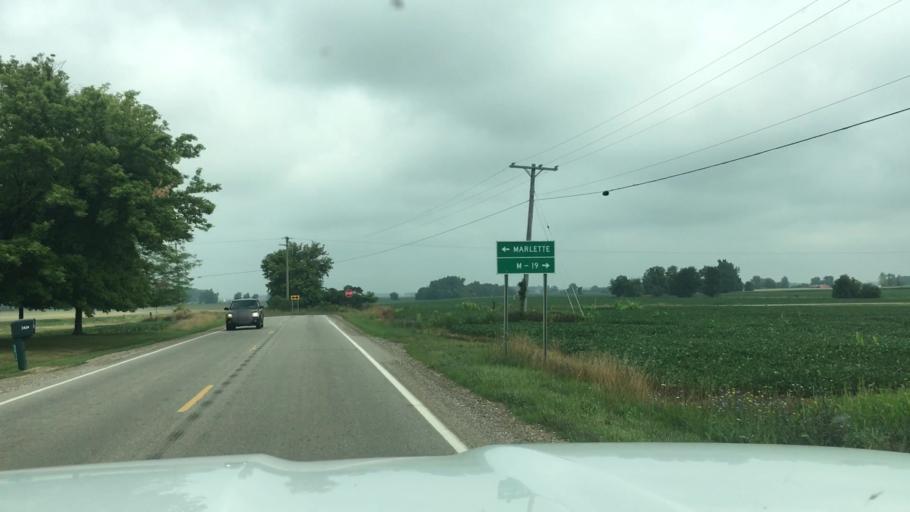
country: US
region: Michigan
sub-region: Sanilac County
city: Marlette
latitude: 43.3289
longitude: -82.9843
